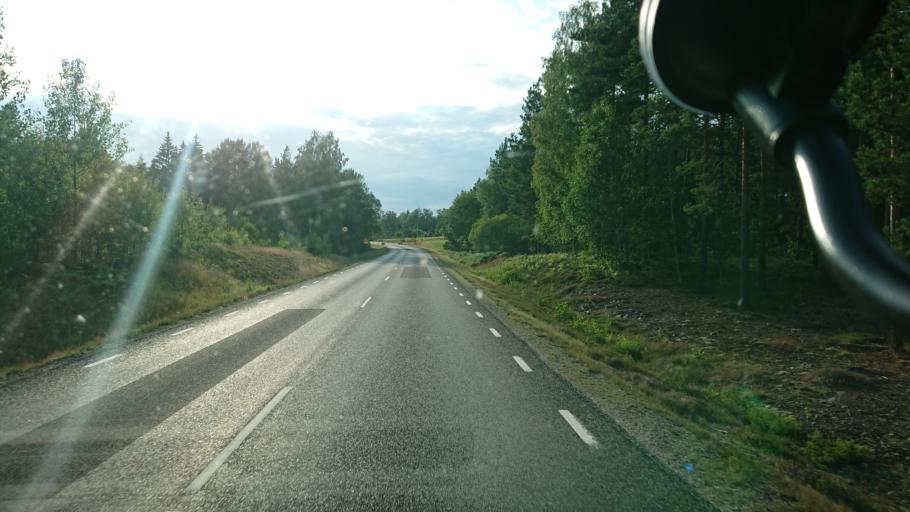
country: SE
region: Kronoberg
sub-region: Vaxjo Kommun
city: Rottne
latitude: 57.0340
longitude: 14.9475
